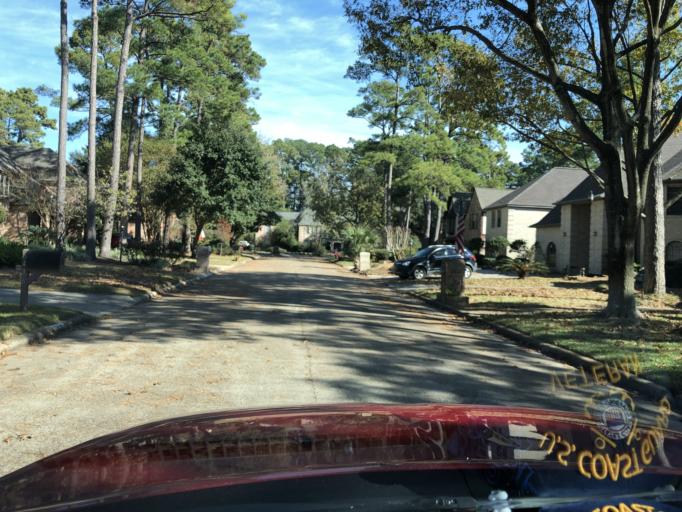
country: US
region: Texas
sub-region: Harris County
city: Tomball
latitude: 30.0217
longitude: -95.5499
